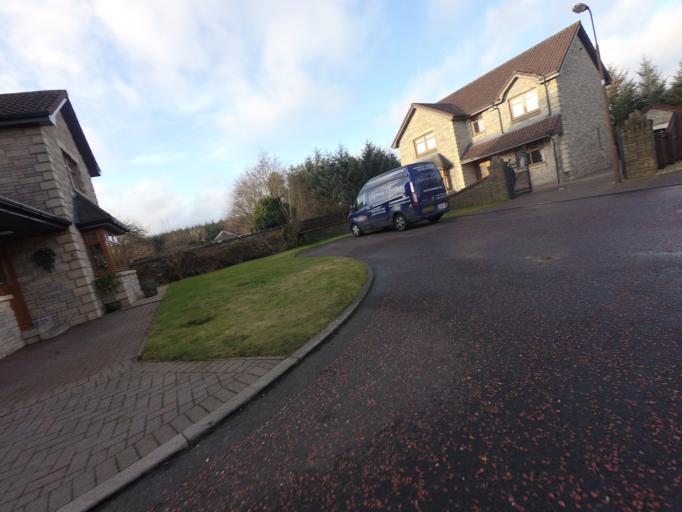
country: GB
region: Scotland
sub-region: West Lothian
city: West Calder
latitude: 55.8765
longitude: -3.5962
